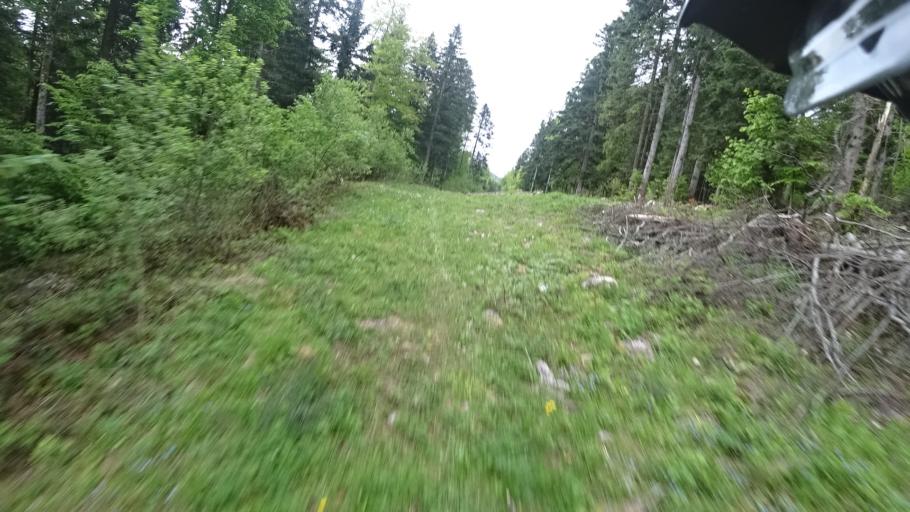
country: HR
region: Karlovacka
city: Plaski
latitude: 44.9664
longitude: 15.4025
